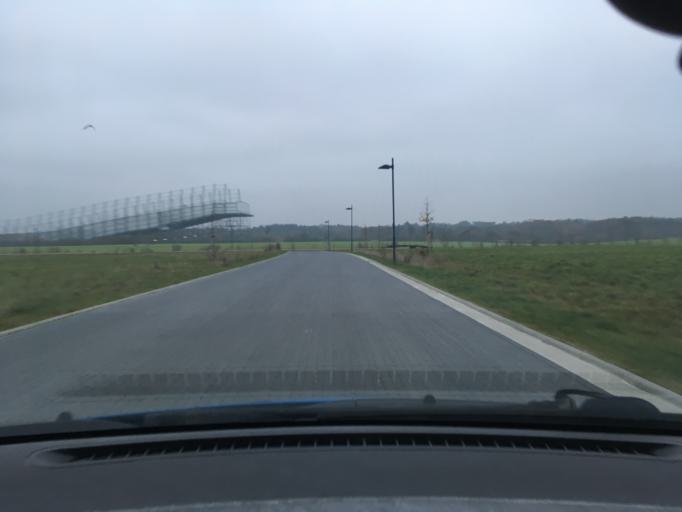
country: DE
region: Lower Saxony
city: Bispingen
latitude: 53.0982
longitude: 9.9863
